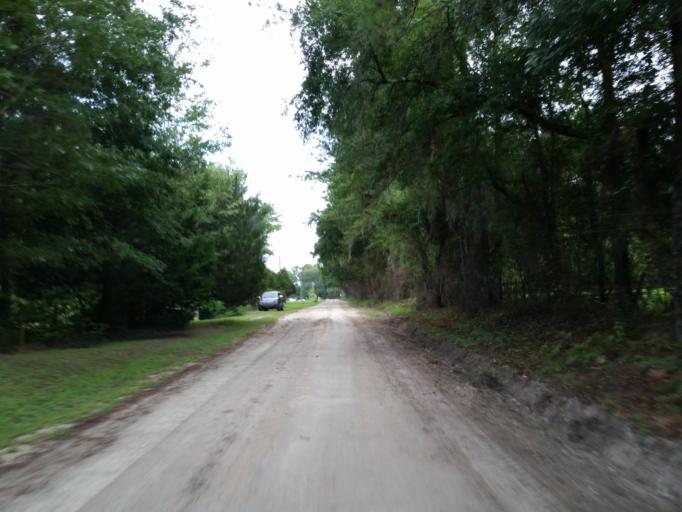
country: US
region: Florida
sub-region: Alachua County
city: High Springs
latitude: 29.9537
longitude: -82.5594
